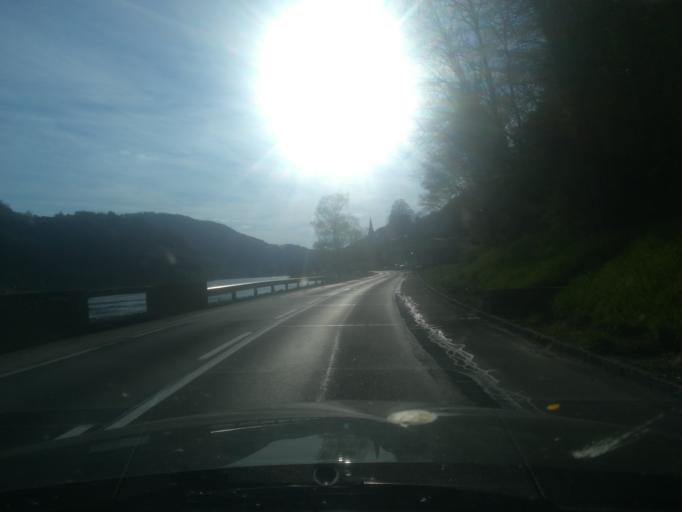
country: AT
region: Lower Austria
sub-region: Politischer Bezirk Melk
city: Nochling
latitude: 48.2334
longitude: 14.9129
